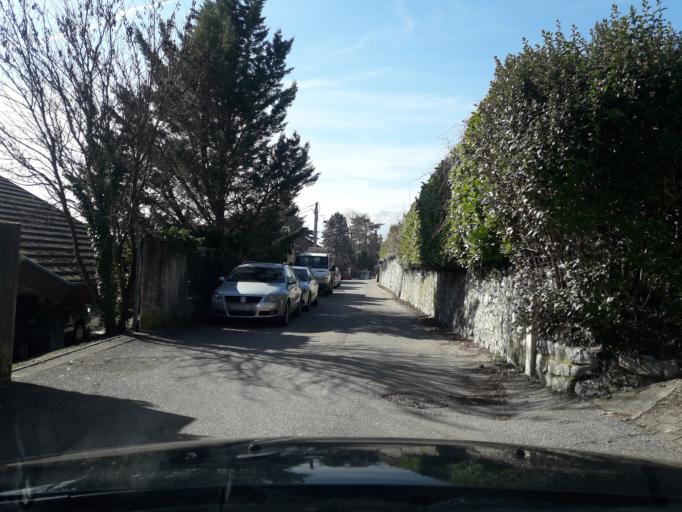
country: FR
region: Rhone-Alpes
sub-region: Departement de l'Isere
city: La Tronche
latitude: 45.2140
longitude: 5.7445
